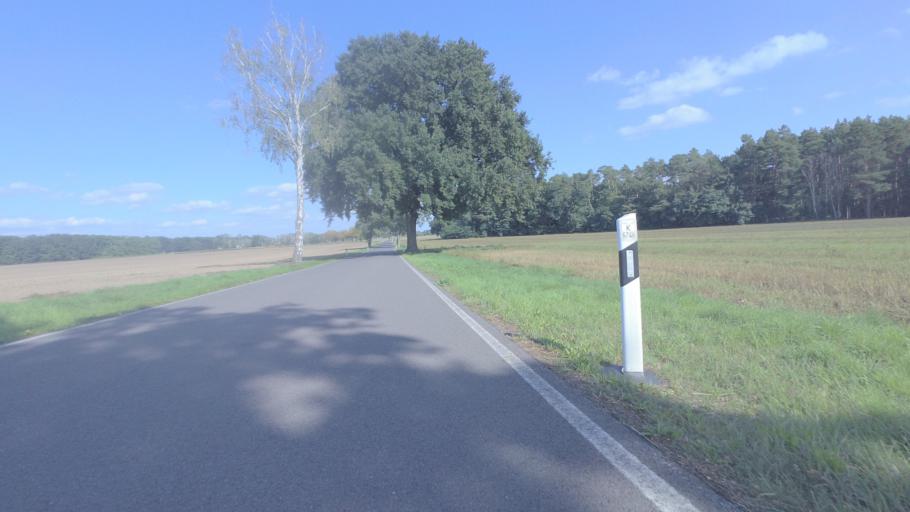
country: DE
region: Brandenburg
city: Munchehofe
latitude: 52.2047
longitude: 13.8628
